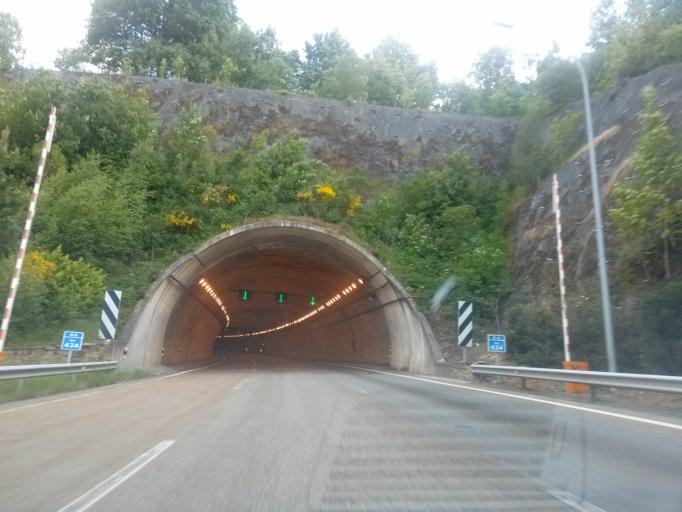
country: ES
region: Castille and Leon
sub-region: Provincia de Leon
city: Balboa
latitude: 42.7360
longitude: -7.0468
